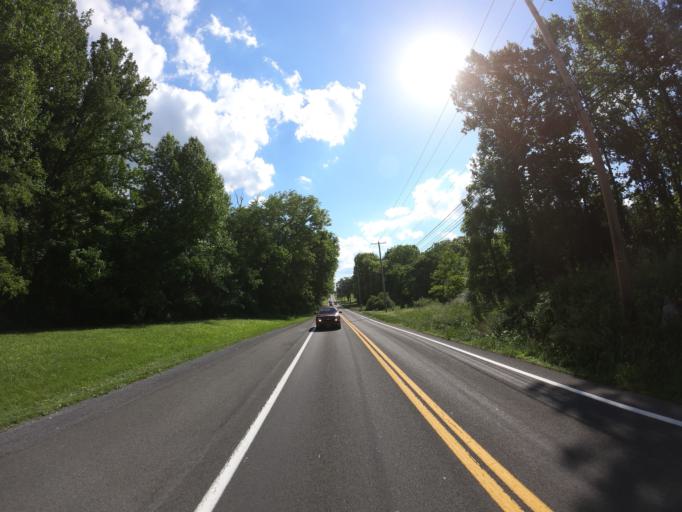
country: US
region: West Virginia
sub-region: Jefferson County
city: Shepherdstown
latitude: 39.4182
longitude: -77.8314
